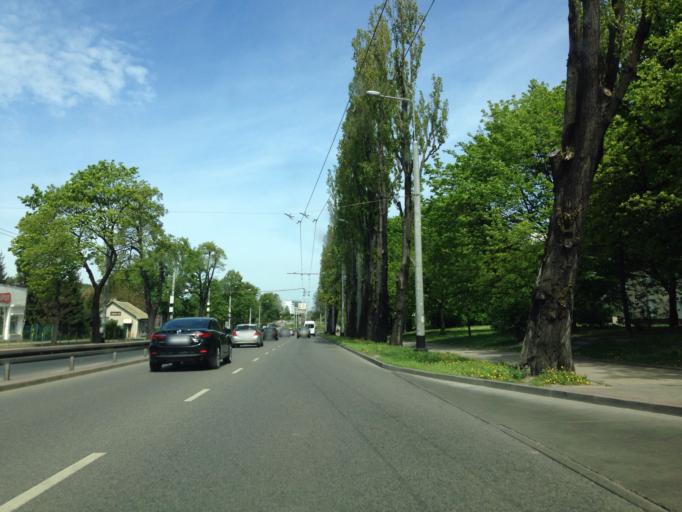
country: PL
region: Pomeranian Voivodeship
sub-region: Gdynia
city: Gdynia
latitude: 54.5034
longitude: 18.5365
